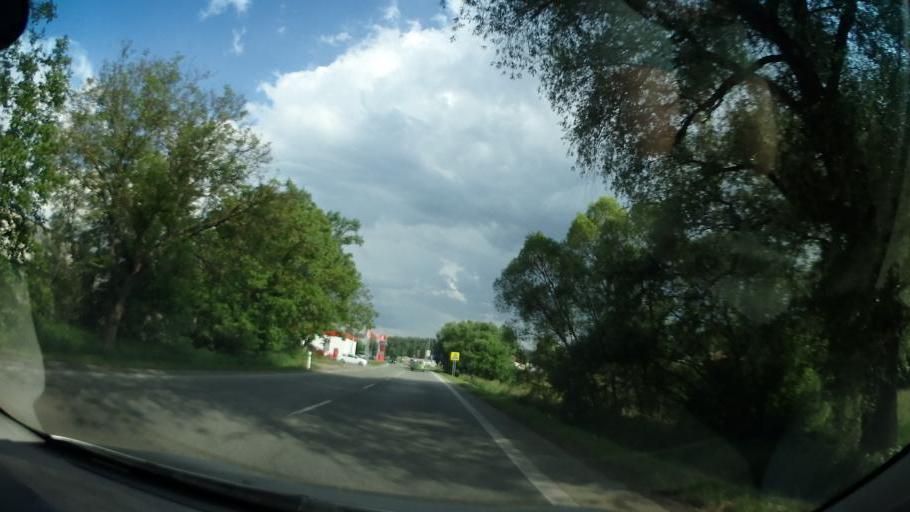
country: CZ
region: South Moravian
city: Tisnov
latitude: 49.3425
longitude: 16.4167
